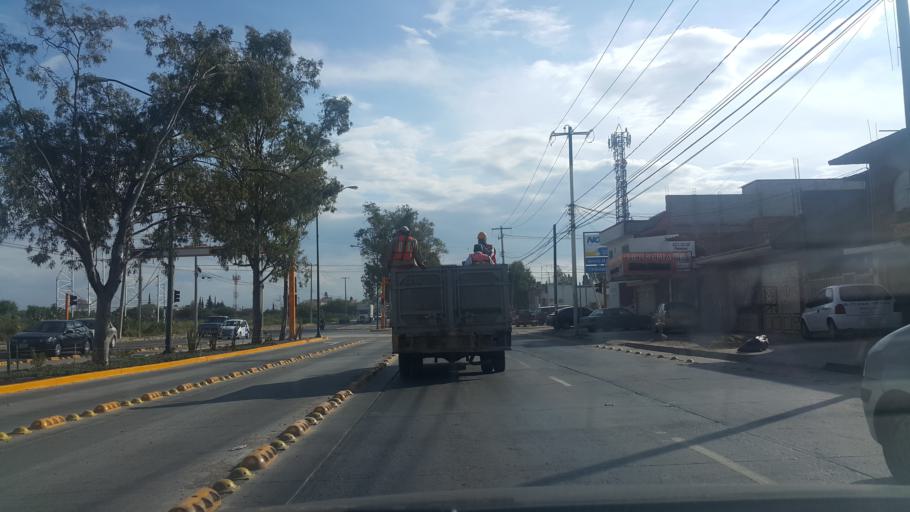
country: MX
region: Guanajuato
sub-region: Leon
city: Medina
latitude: 21.1368
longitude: -101.6422
